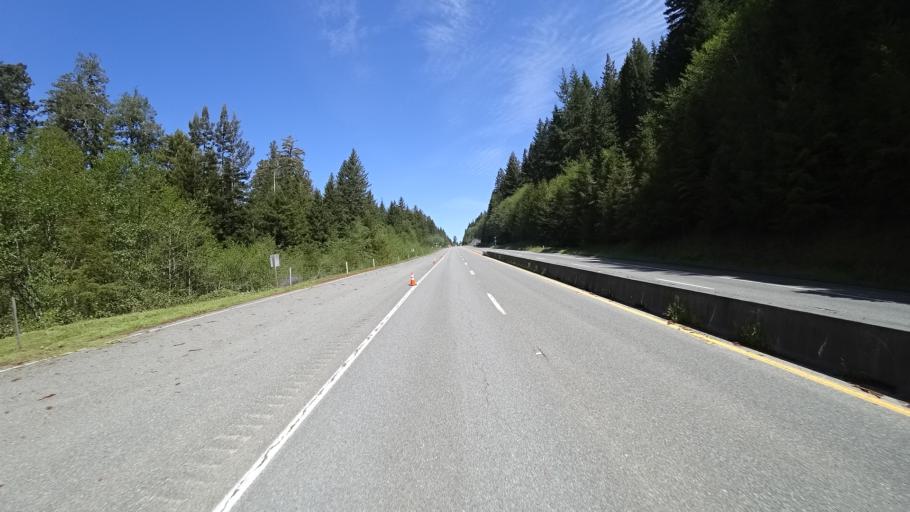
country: US
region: California
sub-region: Humboldt County
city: Westhaven-Moonstone
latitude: 41.3785
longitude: -123.9951
